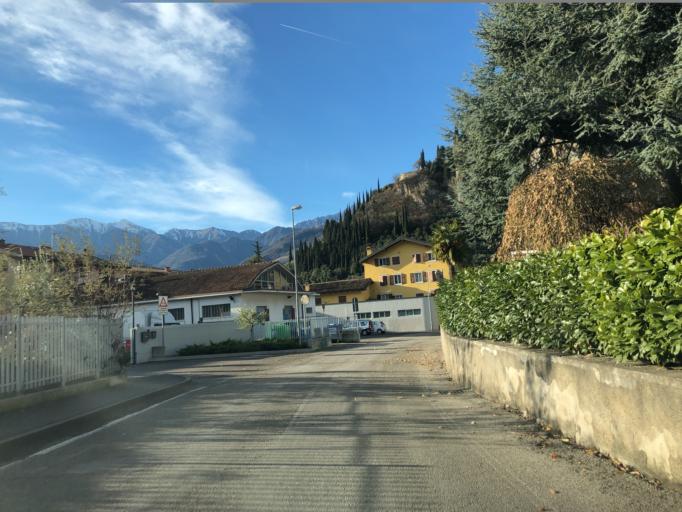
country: IT
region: Trentino-Alto Adige
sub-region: Provincia di Trento
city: Arco
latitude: 45.9198
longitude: 10.8928
